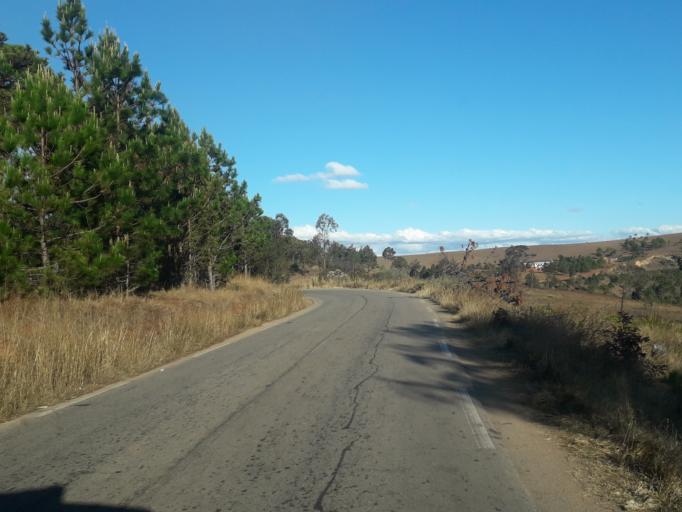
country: MG
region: Analamanga
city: Ankazobe
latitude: -18.0082
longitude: 47.1510
